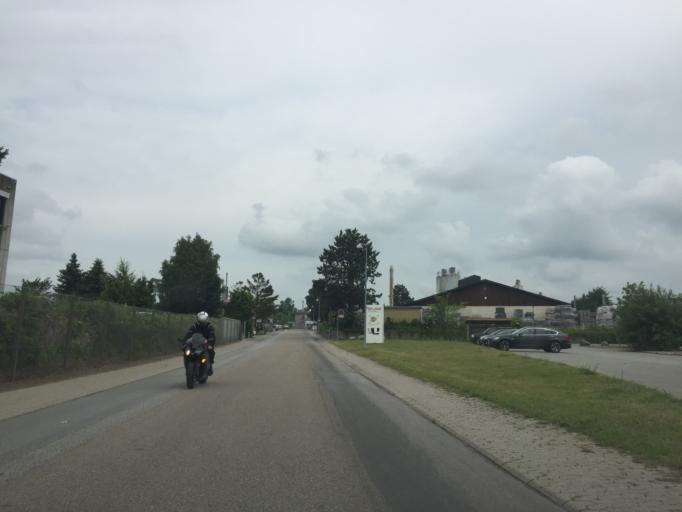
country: DK
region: Capital Region
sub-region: Fureso Kommune
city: Farum
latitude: 55.8197
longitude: 12.3687
